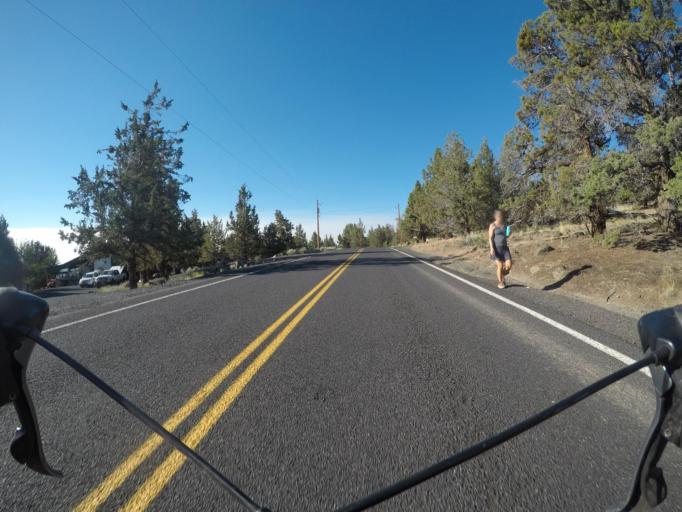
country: US
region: Oregon
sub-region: Deschutes County
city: Bend
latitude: 44.1794
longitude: -121.2662
